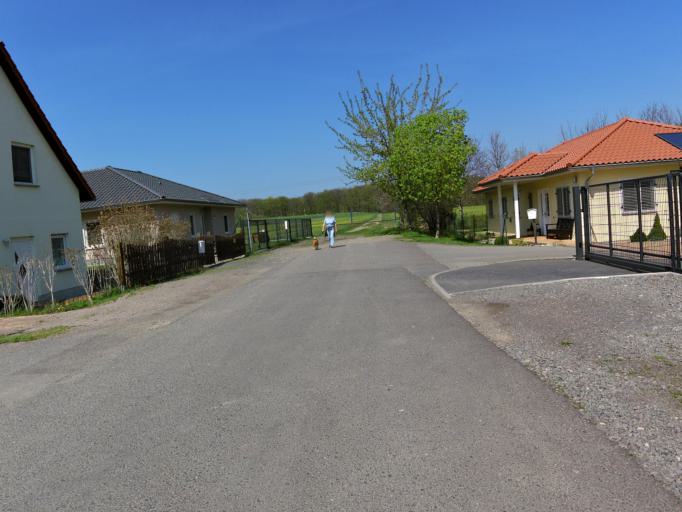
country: DE
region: Saxony
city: Rackwitz
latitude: 51.3949
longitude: 12.3283
